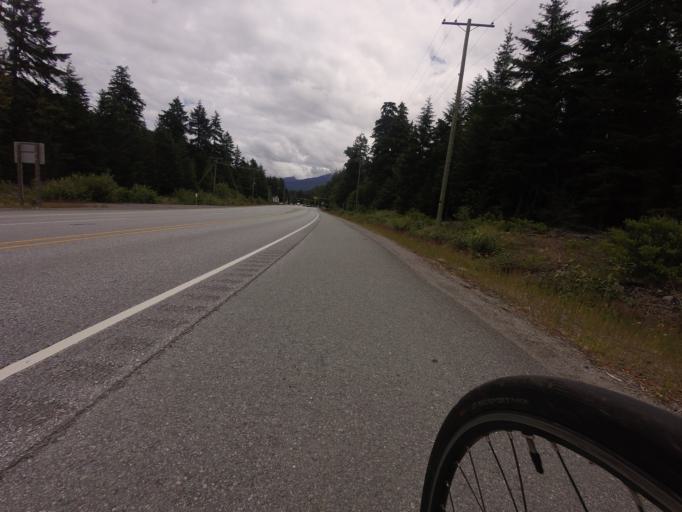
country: CA
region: British Columbia
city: Whistler
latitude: 50.0859
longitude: -123.0408
